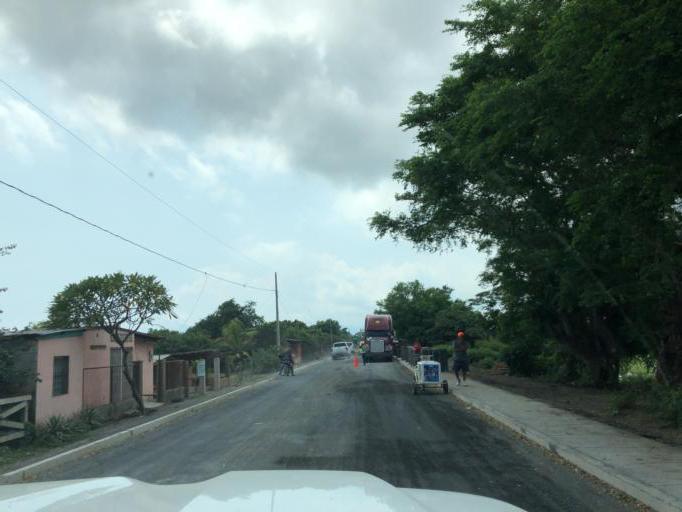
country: NI
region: Granada
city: Granada
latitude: 12.0231
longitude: -85.9281
